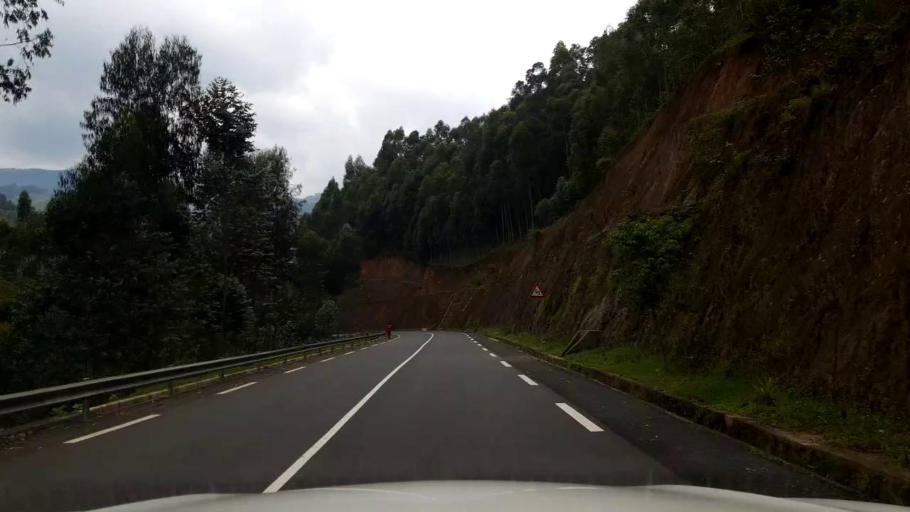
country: RW
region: Western Province
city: Kibuye
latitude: -1.9087
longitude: 29.3642
